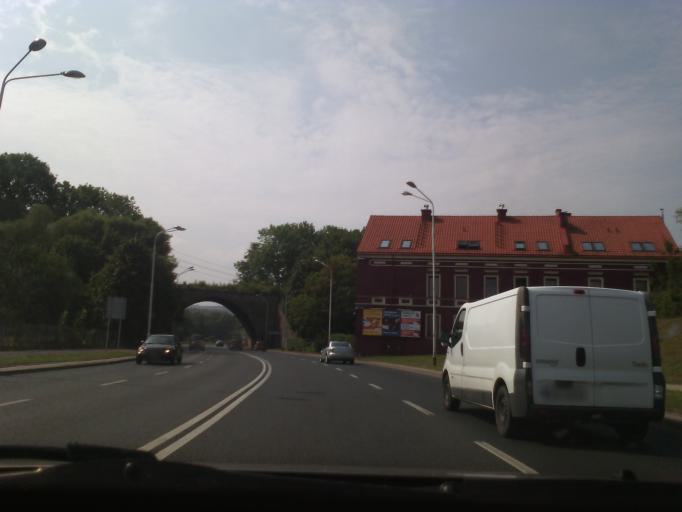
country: PL
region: Lower Silesian Voivodeship
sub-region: Powiat walbrzyski
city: Szczawno-Zdroj
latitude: 50.8177
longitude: 16.2775
